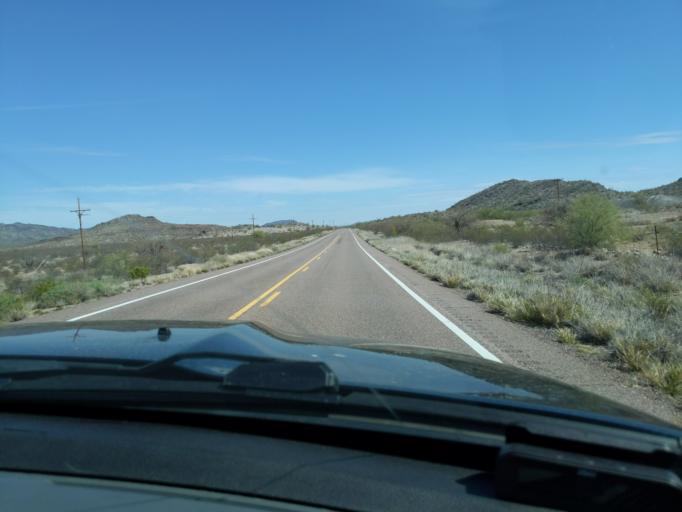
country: US
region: Arizona
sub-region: Pinal County
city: Arizona City
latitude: 32.5997
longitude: -111.9004
